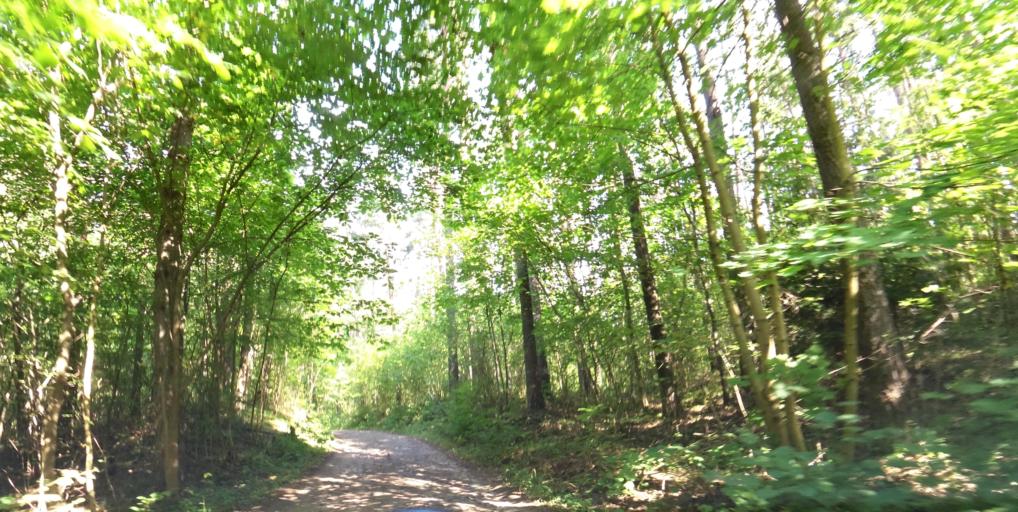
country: LT
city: Grigiskes
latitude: 54.7398
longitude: 25.0329
